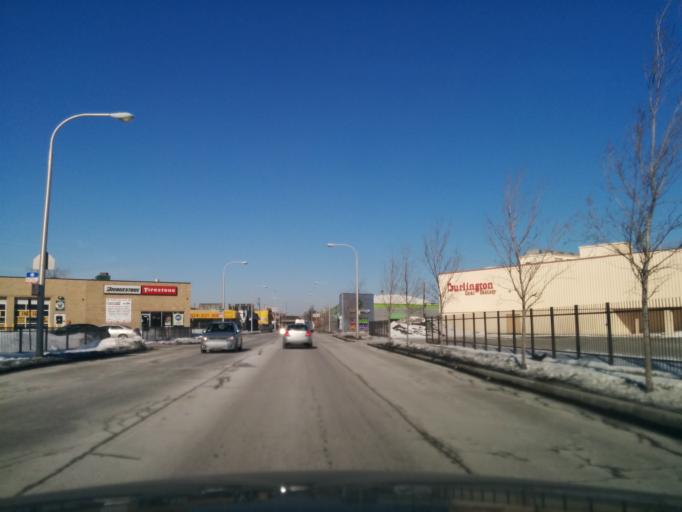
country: US
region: Illinois
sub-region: Cook County
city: Oak Park
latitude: 41.9106
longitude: -87.7374
